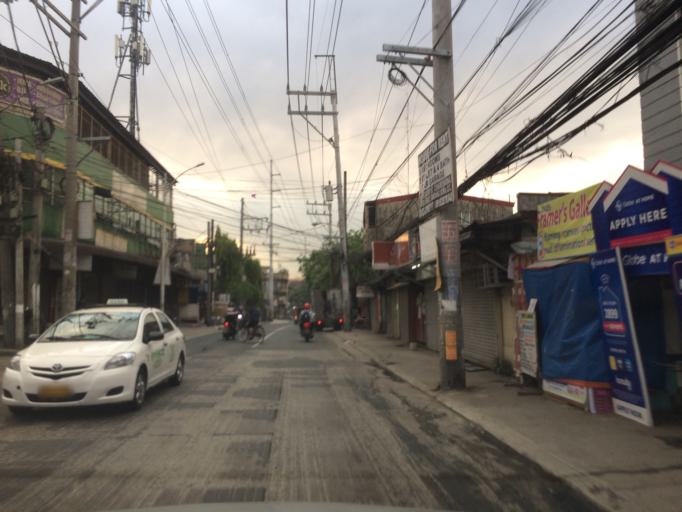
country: PH
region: Calabarzon
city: Bagong Pagasa
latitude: 14.6767
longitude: 121.0352
